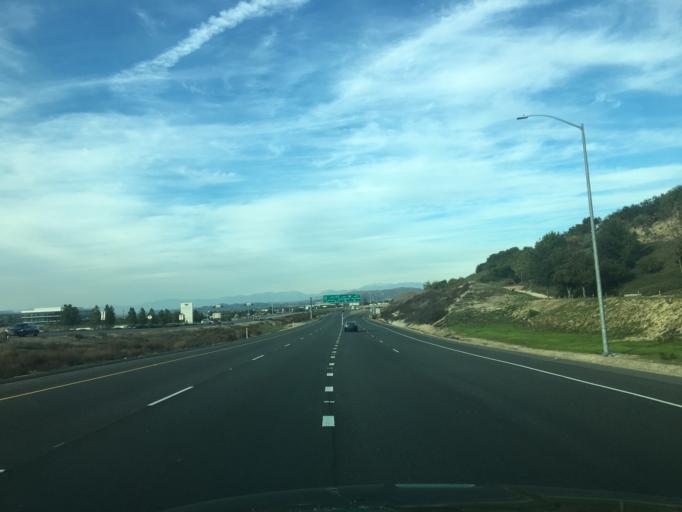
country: US
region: California
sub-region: Orange County
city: Laguna Woods
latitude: 33.6451
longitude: -117.7621
